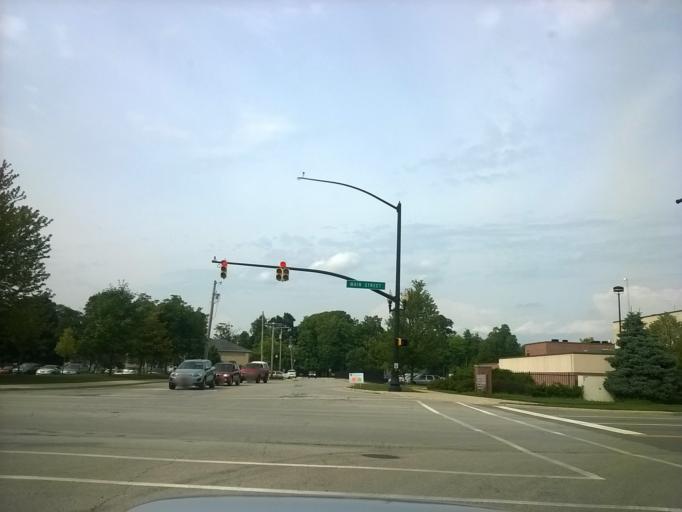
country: US
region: Indiana
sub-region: Hamilton County
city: Carmel
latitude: 39.9783
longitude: -86.1226
